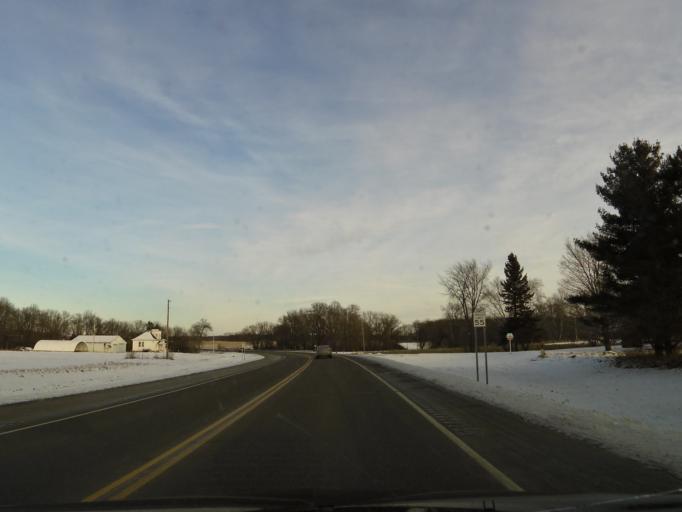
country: US
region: Wisconsin
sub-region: Polk County
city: Osceola
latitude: 45.3110
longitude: -92.7506
